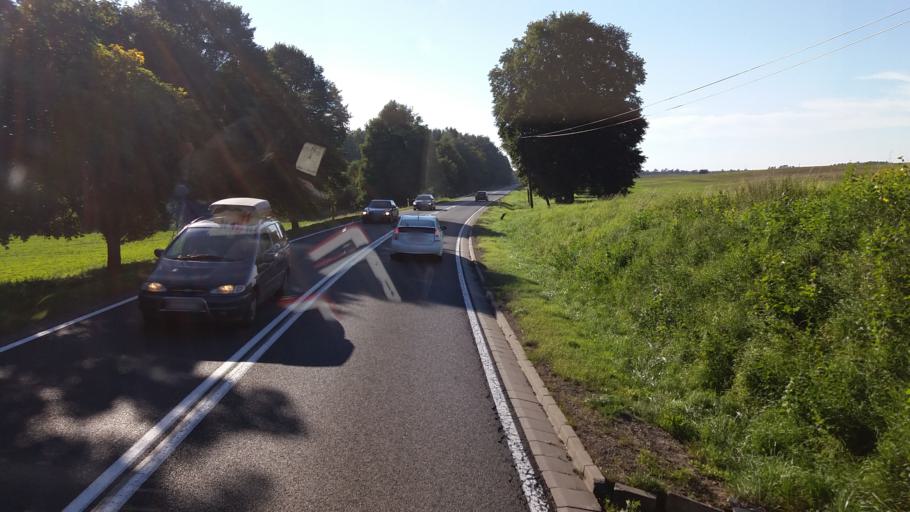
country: PL
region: West Pomeranian Voivodeship
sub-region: Powiat drawski
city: Kalisz Pomorski
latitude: 53.2964
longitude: 15.8322
